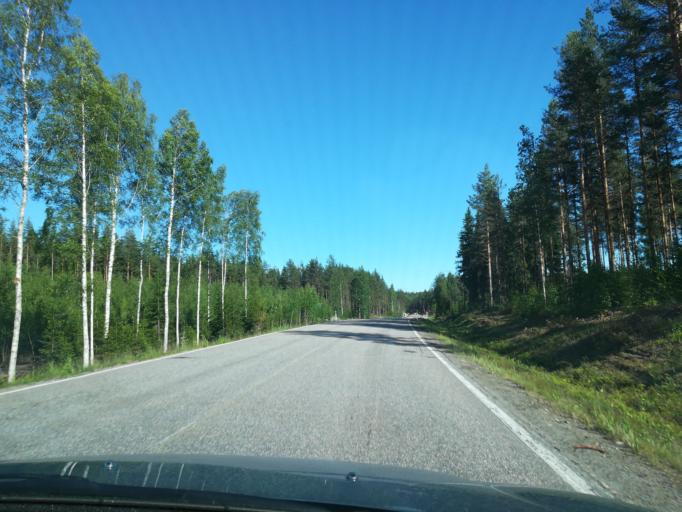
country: FI
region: Southern Savonia
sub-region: Mikkeli
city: Puumala
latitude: 61.4701
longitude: 28.3117
